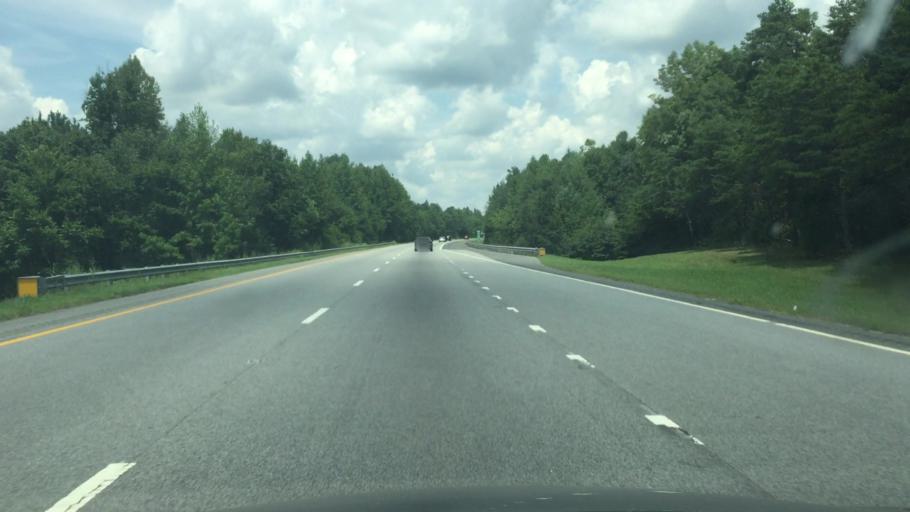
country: US
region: North Carolina
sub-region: Guilford County
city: Pleasant Garden
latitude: 35.9282
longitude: -79.8268
